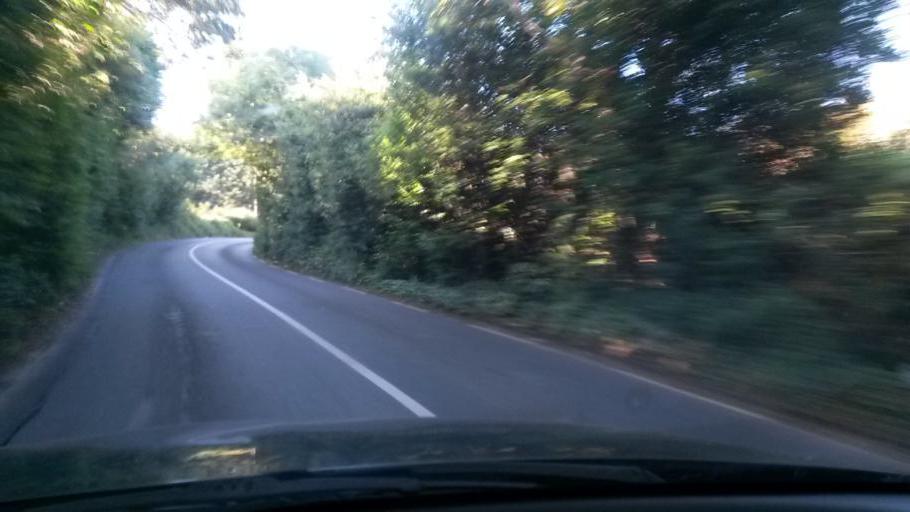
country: IE
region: Leinster
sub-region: Fingal County
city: Blanchardstown
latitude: 53.4325
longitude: -6.3613
